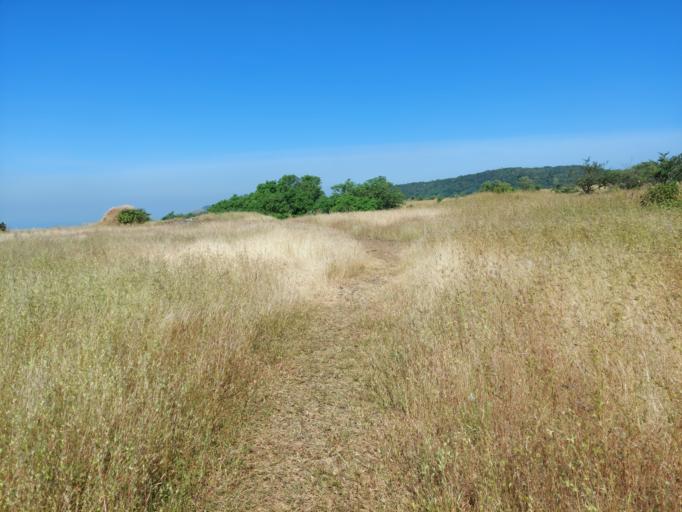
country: IN
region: Maharashtra
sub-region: Sindhudurg
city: Kudal
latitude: 16.0803
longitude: 73.8439
